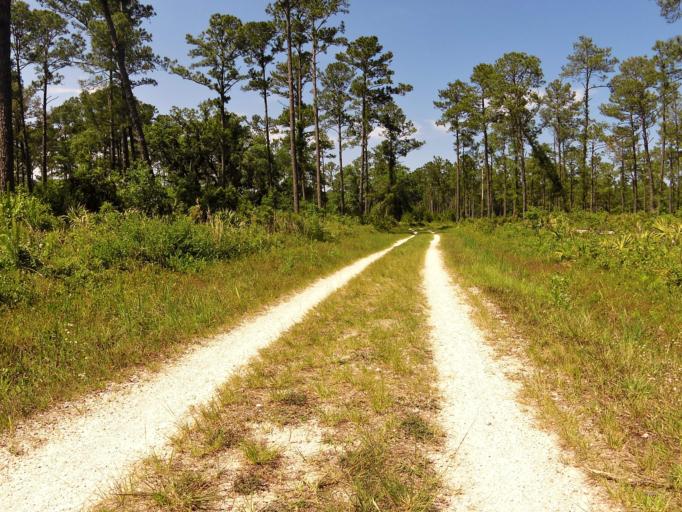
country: US
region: Florida
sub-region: Saint Johns County
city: Palm Valley
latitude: 30.1344
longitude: -81.3782
